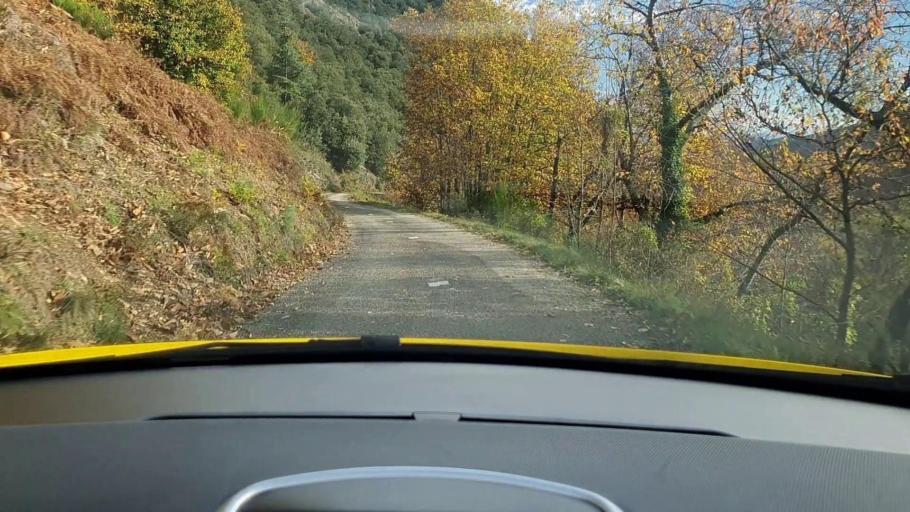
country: FR
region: Languedoc-Roussillon
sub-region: Departement du Gard
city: Valleraugue
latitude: 44.0836
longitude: 3.7332
